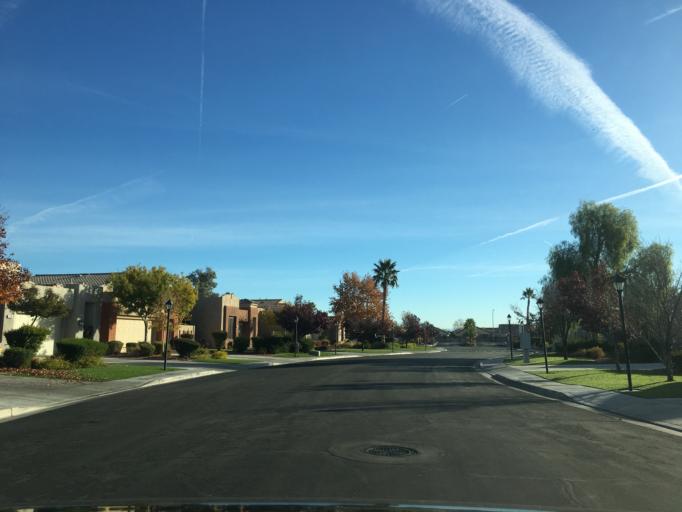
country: US
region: Nevada
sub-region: Clark County
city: Enterprise
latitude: 36.0227
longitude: -115.1653
